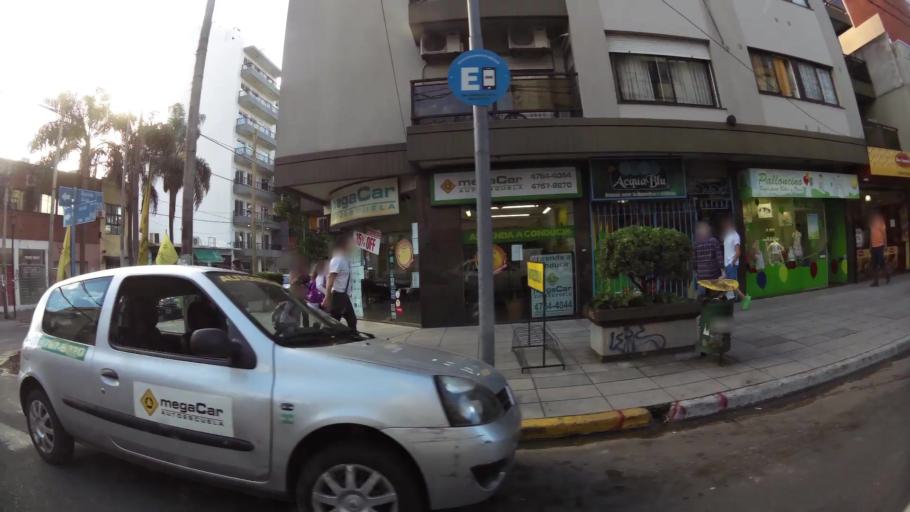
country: AR
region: Buenos Aires
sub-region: Partido de General San Martin
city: General San Martin
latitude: -34.5472
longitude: -58.5514
